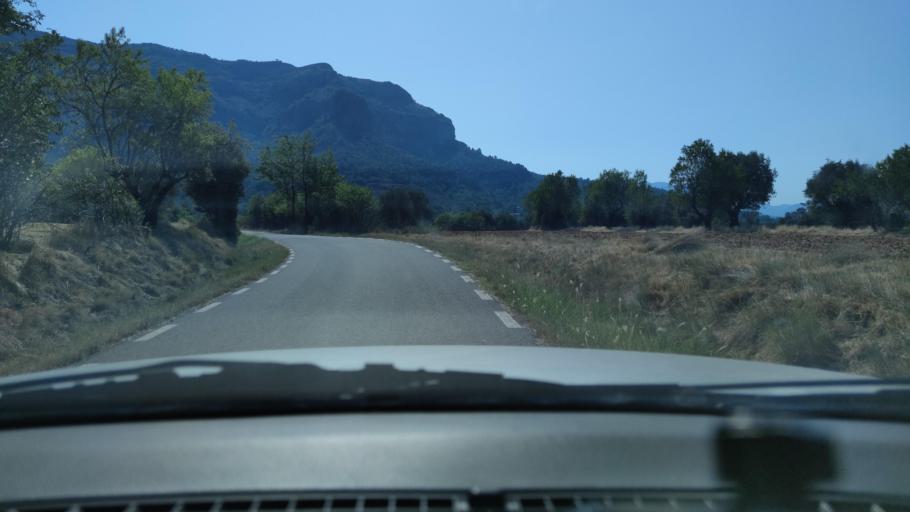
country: ES
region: Catalonia
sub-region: Provincia de Lleida
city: Senterada
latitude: 42.2759
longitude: 0.9440
